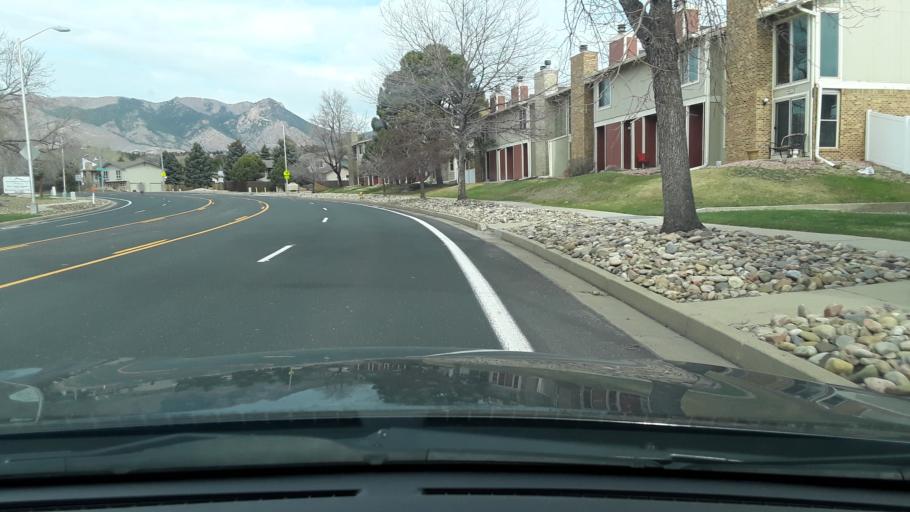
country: US
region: Colorado
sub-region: El Paso County
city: Air Force Academy
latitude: 38.9288
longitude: -104.8338
